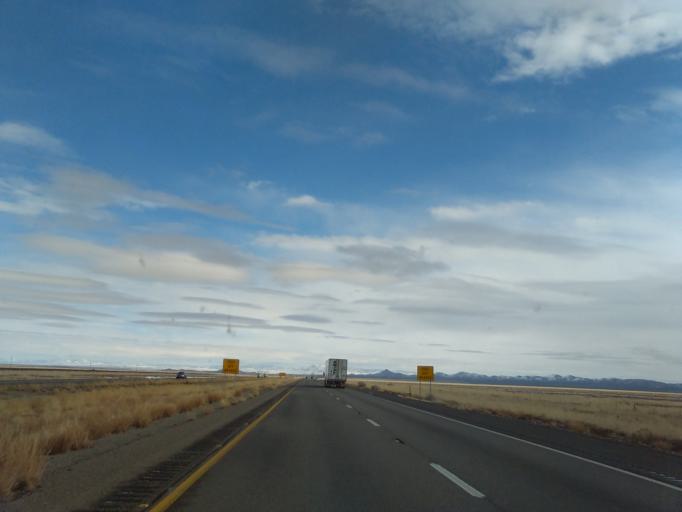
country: US
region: New Mexico
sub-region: Hidalgo County
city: Lordsburg
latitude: 32.2604
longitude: -108.9145
